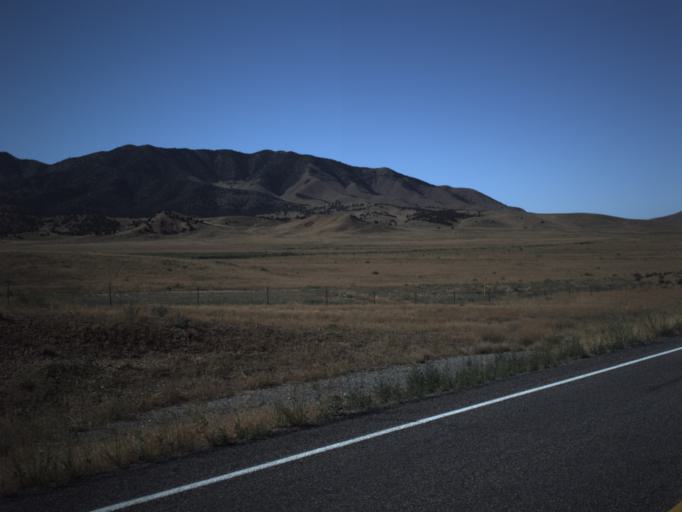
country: US
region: Utah
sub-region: Juab County
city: Nephi
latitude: 39.6821
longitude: -112.2494
